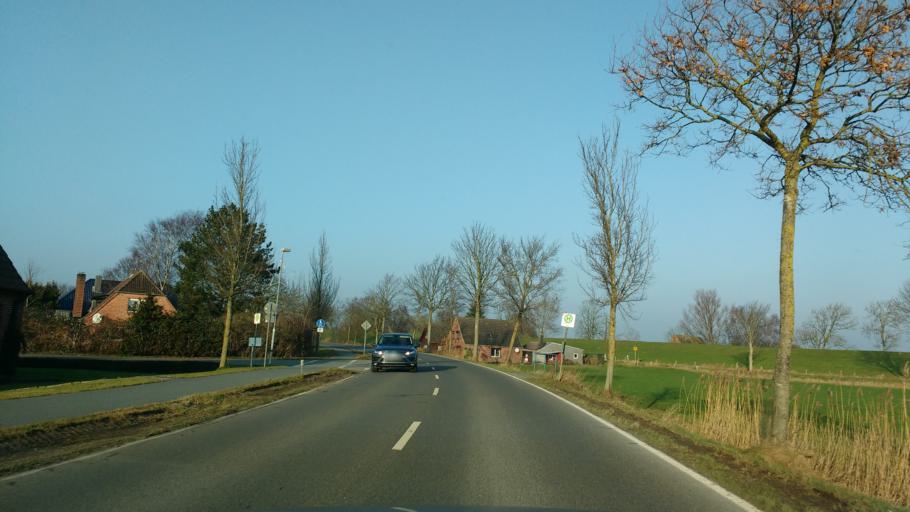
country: DE
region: Schleswig-Holstein
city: Friedrichskoog
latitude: 54.0030
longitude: 8.8873
